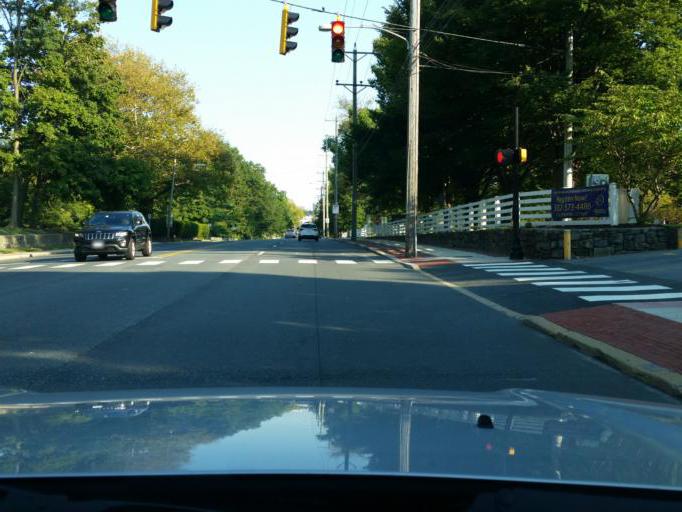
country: US
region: Delaware
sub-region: New Castle County
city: Greenville
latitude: 39.7619
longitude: -75.5780
